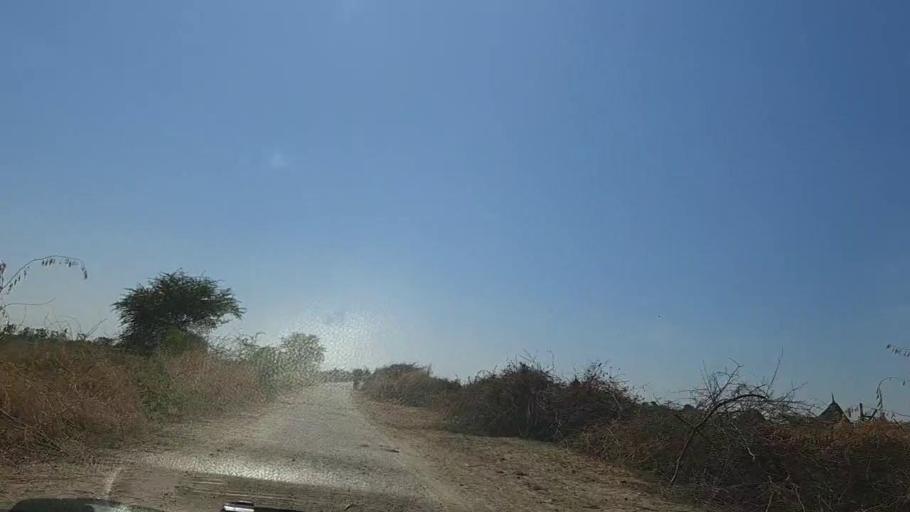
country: PK
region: Sindh
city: Dhoro Naro
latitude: 25.4843
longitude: 69.5424
